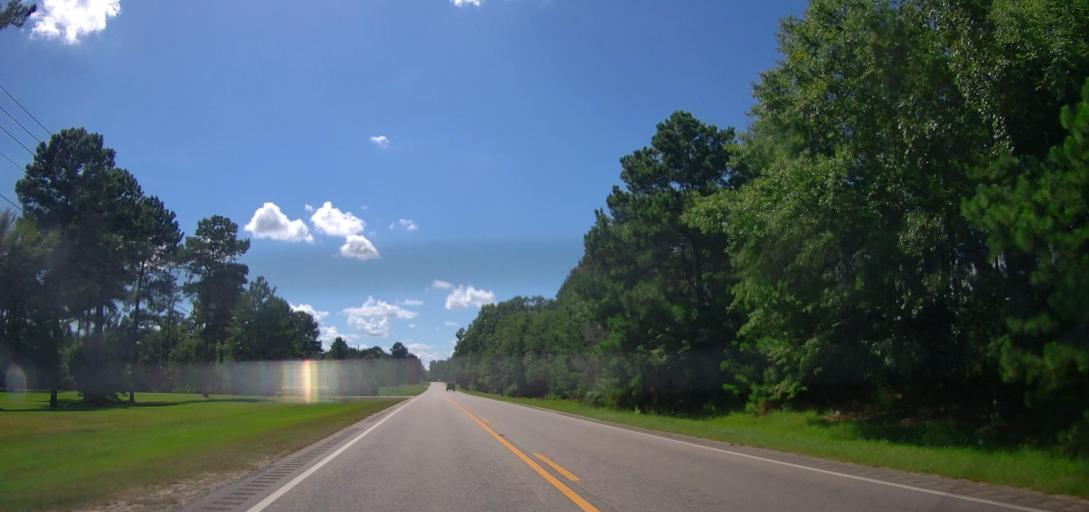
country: US
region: Alabama
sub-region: Elmore County
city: Tallassee
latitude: 32.3766
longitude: -85.8523
